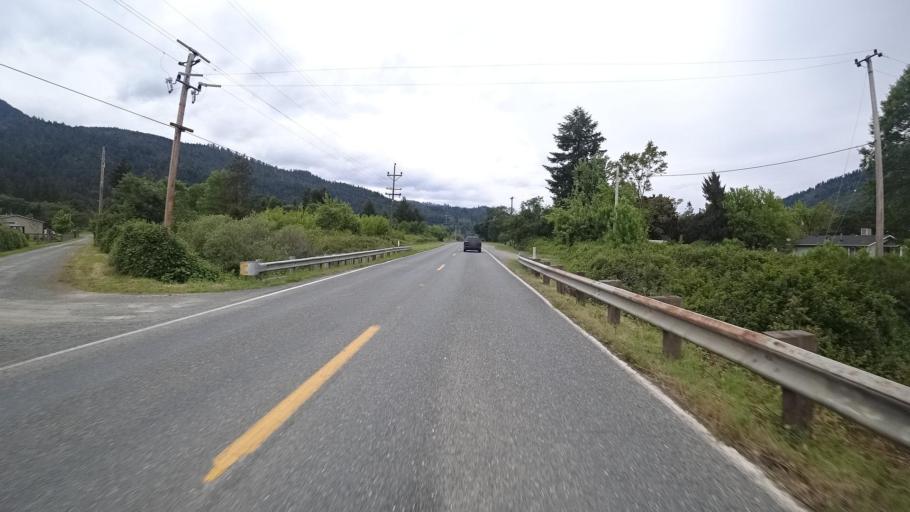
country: US
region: California
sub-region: Humboldt County
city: Willow Creek
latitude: 41.0263
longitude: -123.6557
